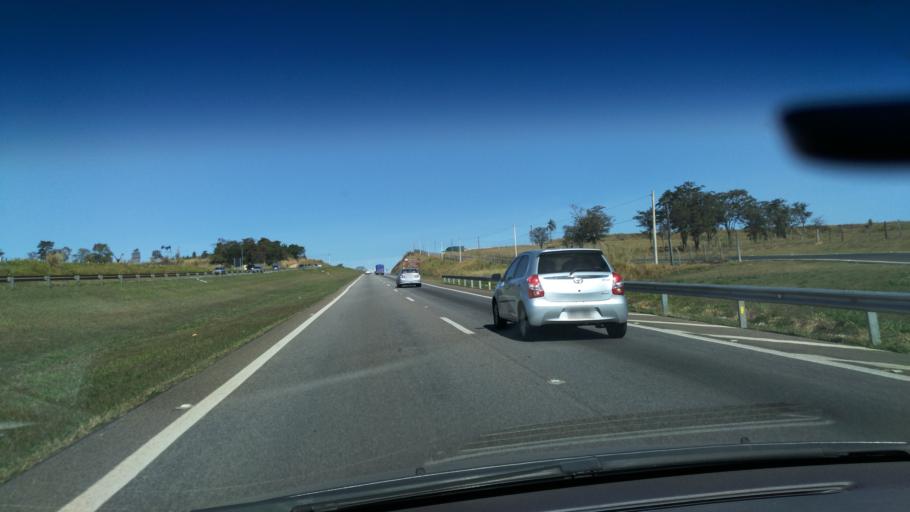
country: BR
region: Sao Paulo
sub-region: Jaguariuna
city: Jaguariuna
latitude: -22.6668
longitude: -47.0030
